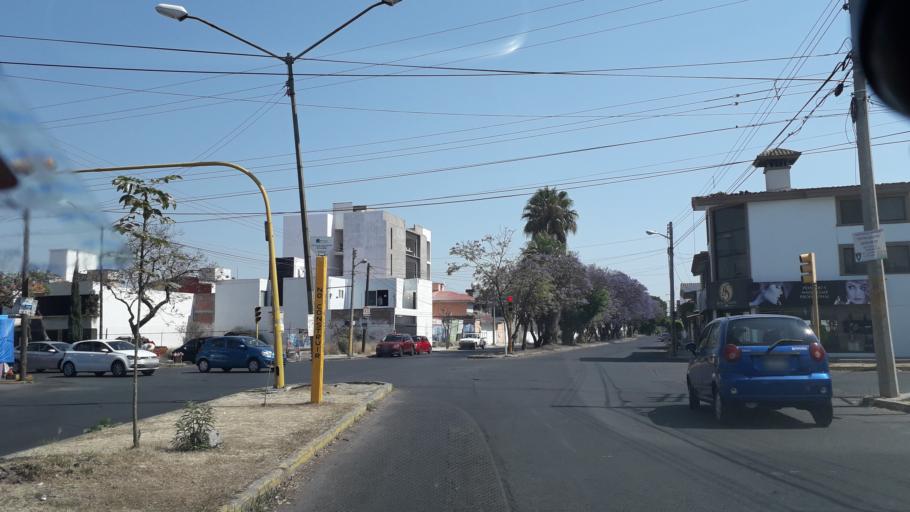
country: MX
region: Puebla
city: Puebla
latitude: 19.0173
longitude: -98.1954
